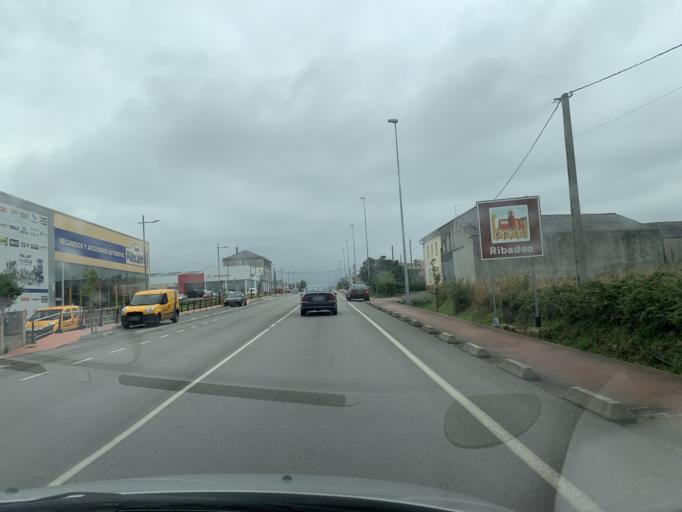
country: ES
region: Galicia
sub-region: Provincia de Lugo
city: Ribadeo
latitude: 43.5407
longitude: -7.0663
